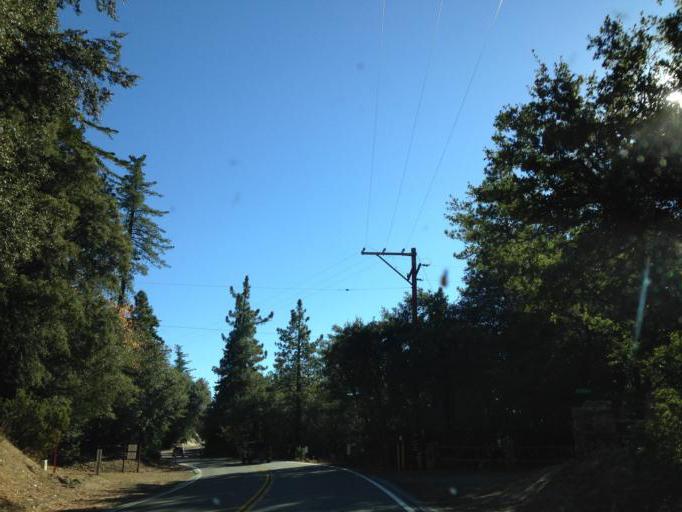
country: US
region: California
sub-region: Riverside County
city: Idyllwild-Pine Cove
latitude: 33.7708
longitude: -116.7409
